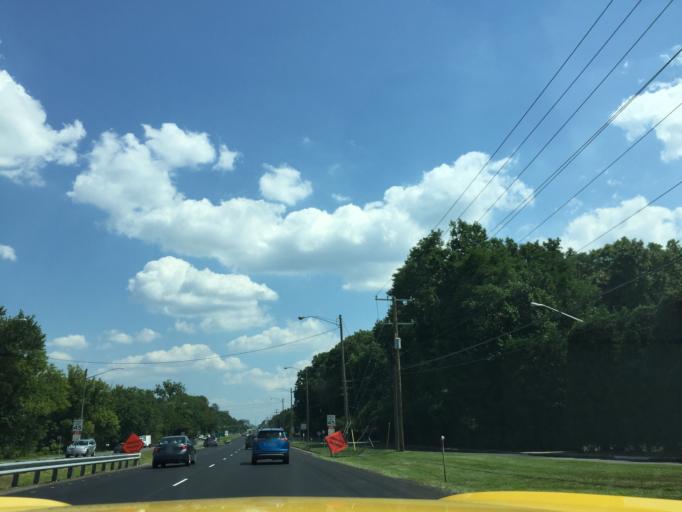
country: US
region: Virginia
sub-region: Fairfax County
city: Wolf Trap
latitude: 38.9464
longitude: -77.2589
